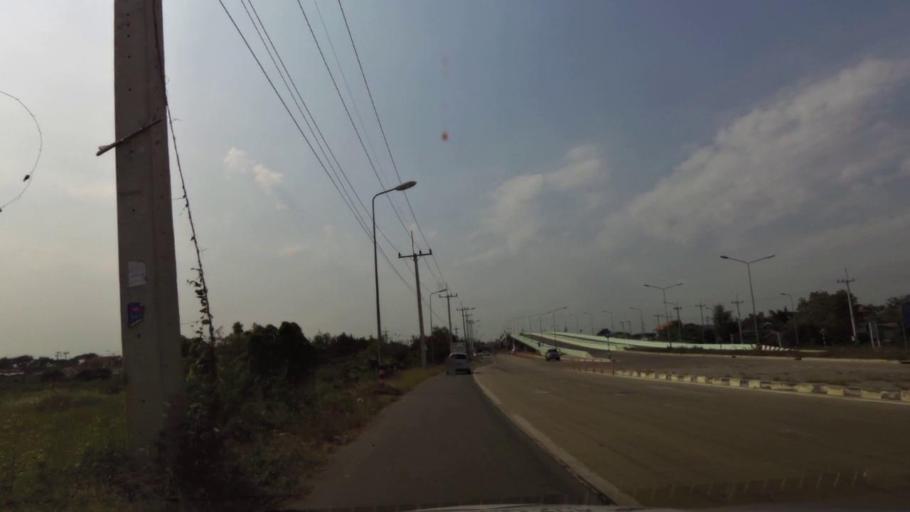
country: TH
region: Phra Nakhon Si Ayutthaya
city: Phra Nakhon Si Ayutthaya
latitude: 14.3291
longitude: 100.5797
